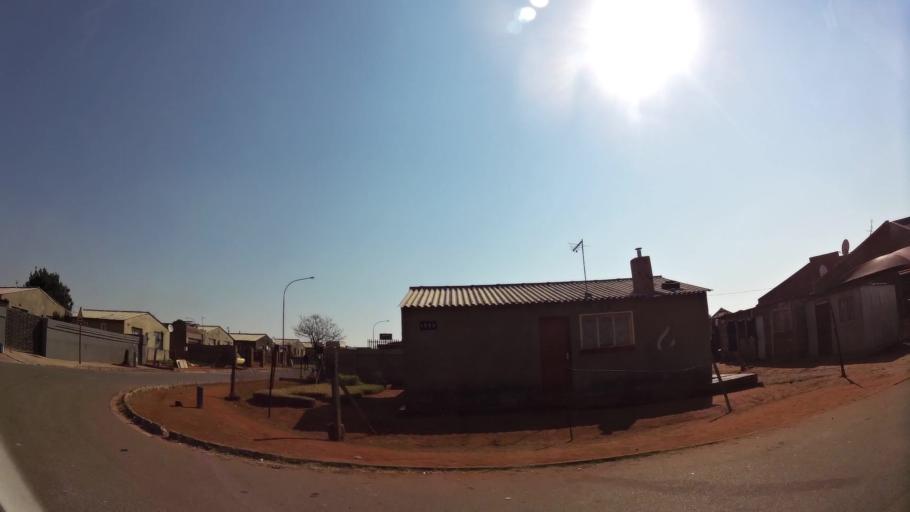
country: ZA
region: Gauteng
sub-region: Ekurhuleni Metropolitan Municipality
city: Benoni
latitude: -26.2256
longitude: 28.3019
